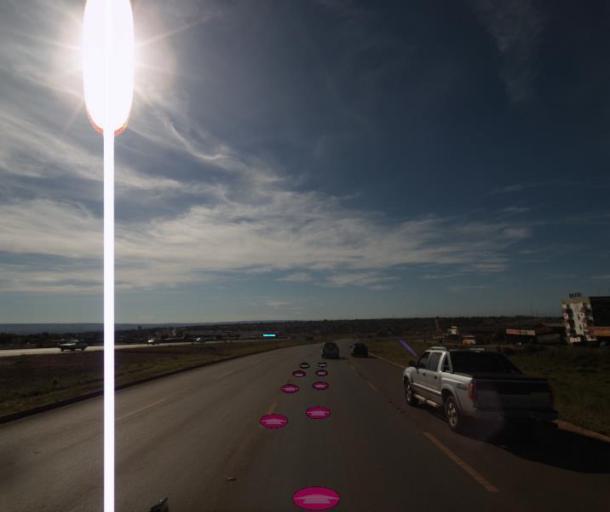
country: BR
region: Federal District
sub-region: Brasilia
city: Brasilia
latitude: -15.7355
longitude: -48.2787
